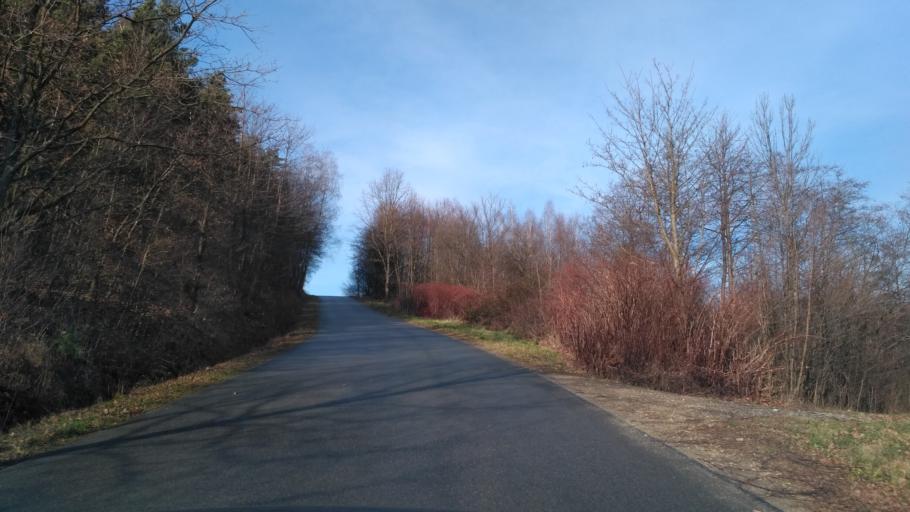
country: PL
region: Subcarpathian Voivodeship
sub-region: Powiat krosnienski
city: Korczyna
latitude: 49.7287
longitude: 21.7915
